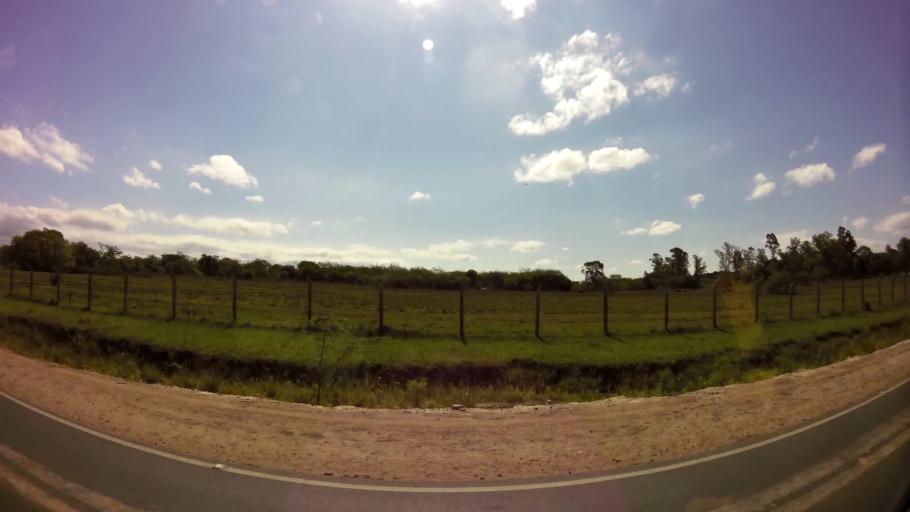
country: PY
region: Central
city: Fernando de la Mora
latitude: -25.2789
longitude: -57.5240
